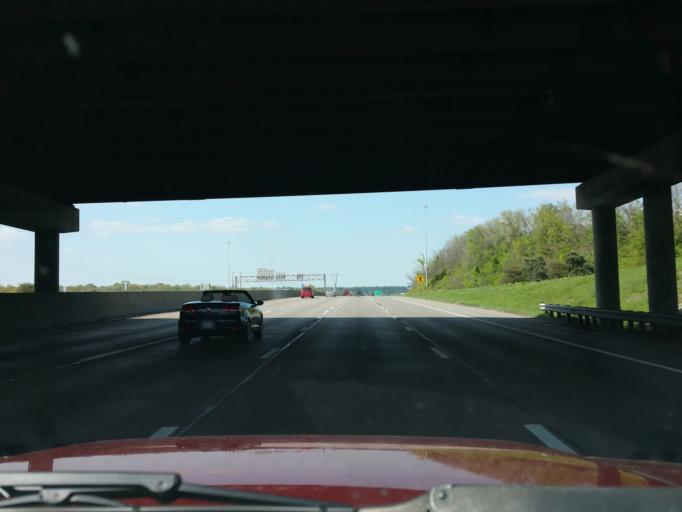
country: US
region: Kansas
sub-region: Johnson County
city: Merriam
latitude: 39.0148
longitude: -94.6930
